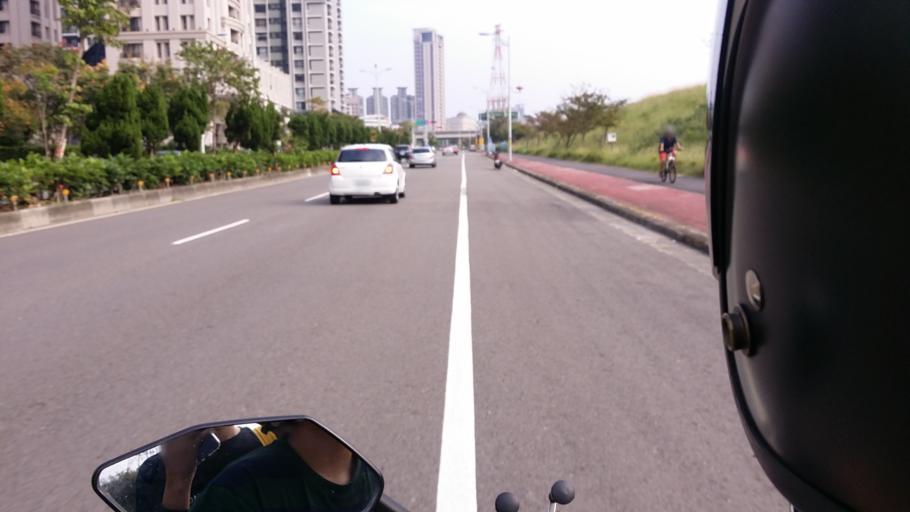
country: TW
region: Taiwan
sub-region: Hsinchu
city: Zhubei
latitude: 24.8188
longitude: 121.0096
